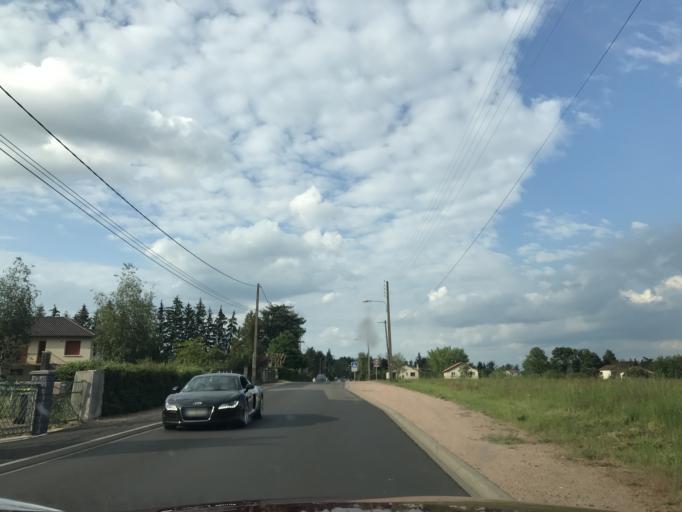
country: FR
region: Auvergne
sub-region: Departement du Puy-de-Dome
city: Lezoux
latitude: 45.8399
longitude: 3.3898
